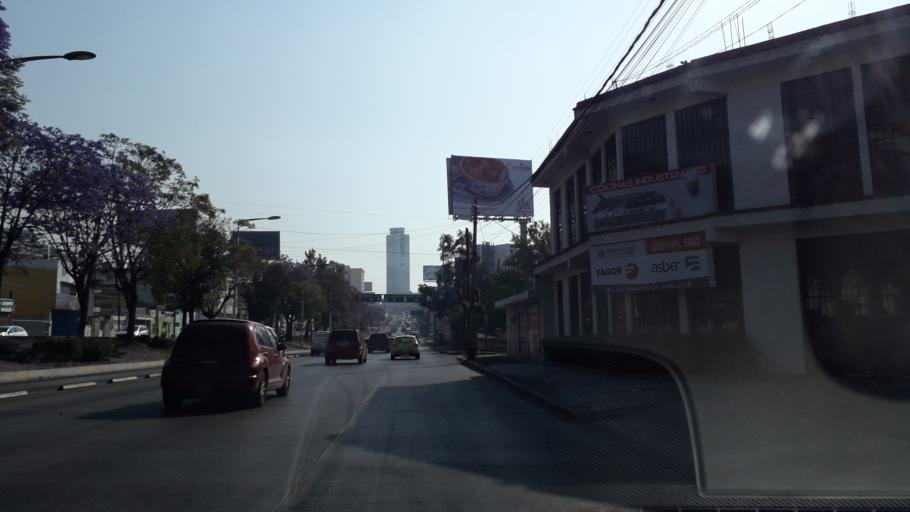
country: MX
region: Puebla
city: Puebla
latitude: 19.0499
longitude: -98.2298
